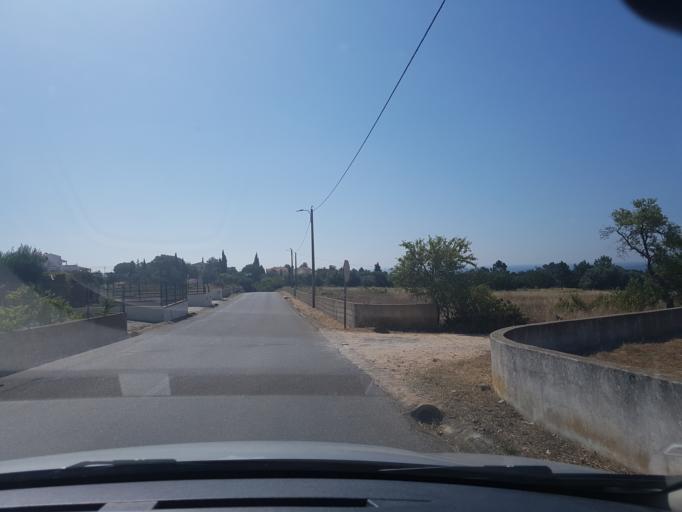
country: PT
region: Faro
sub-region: Lagoa
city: Carvoeiro
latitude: 37.0982
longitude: -8.4228
